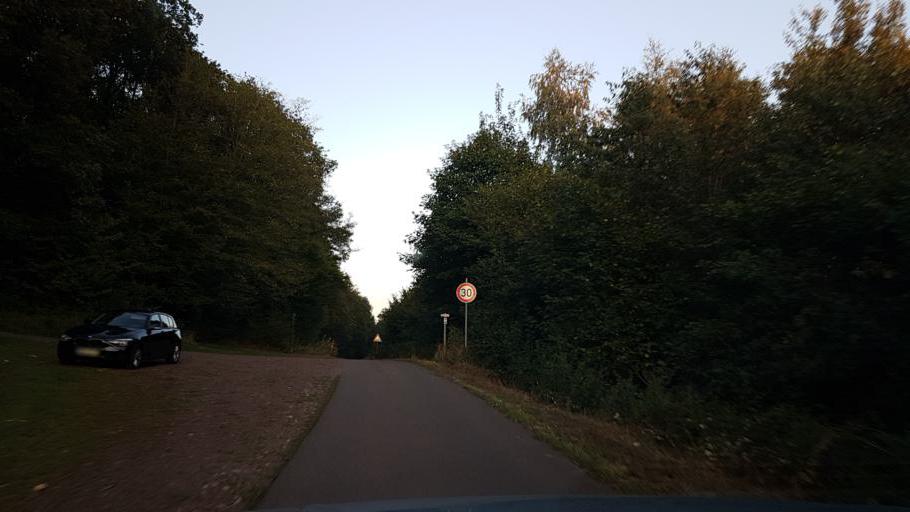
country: DE
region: Saarland
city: Tholey
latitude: 49.4850
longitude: 6.9521
